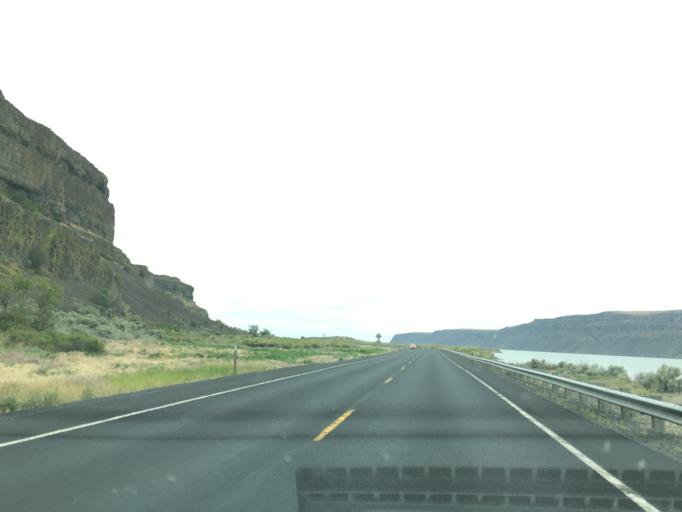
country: US
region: Washington
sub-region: Okanogan County
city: Coulee Dam
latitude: 47.7167
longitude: -119.2601
